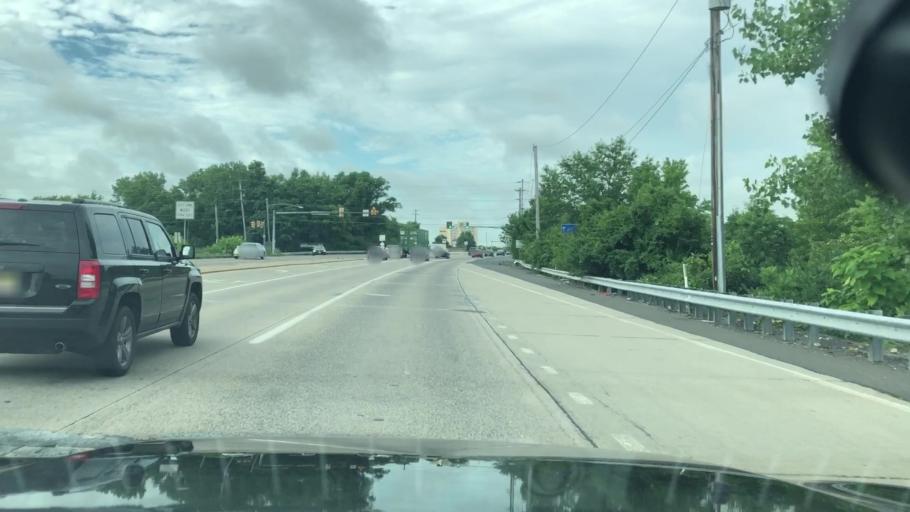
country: US
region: Pennsylvania
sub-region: Bucks County
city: Fairless Hills
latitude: 40.1913
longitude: -74.8656
